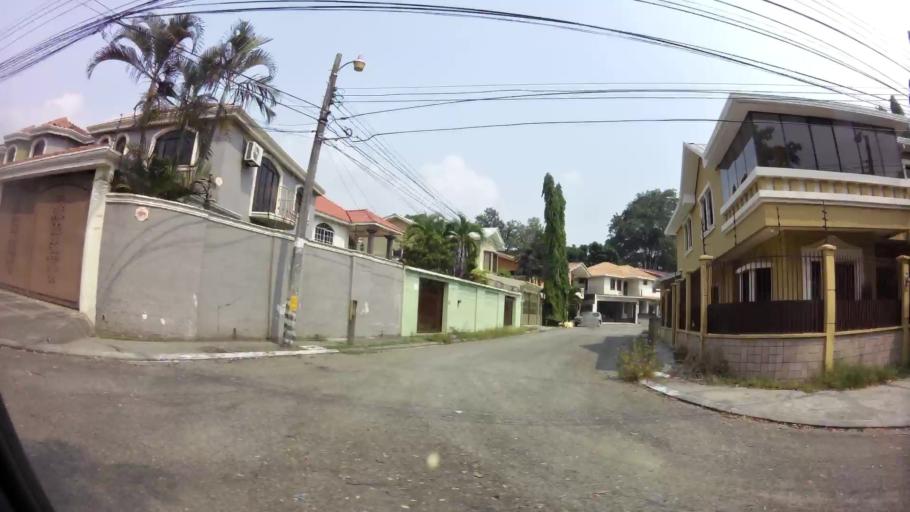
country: HN
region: Cortes
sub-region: San Pedro Sula
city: Pena Blanca
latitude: 15.5561
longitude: -88.0196
